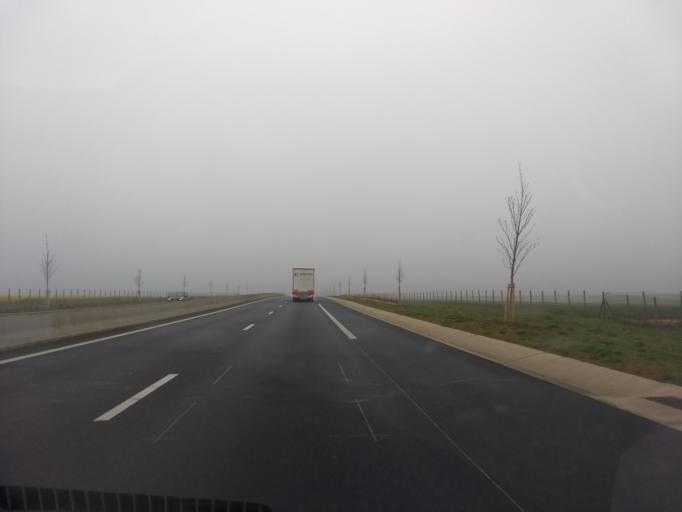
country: FR
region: Nord-Pas-de-Calais
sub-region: Departement du Pas-de-Calais
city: Aubigny-en-Artois
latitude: 50.3398
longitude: 2.6061
